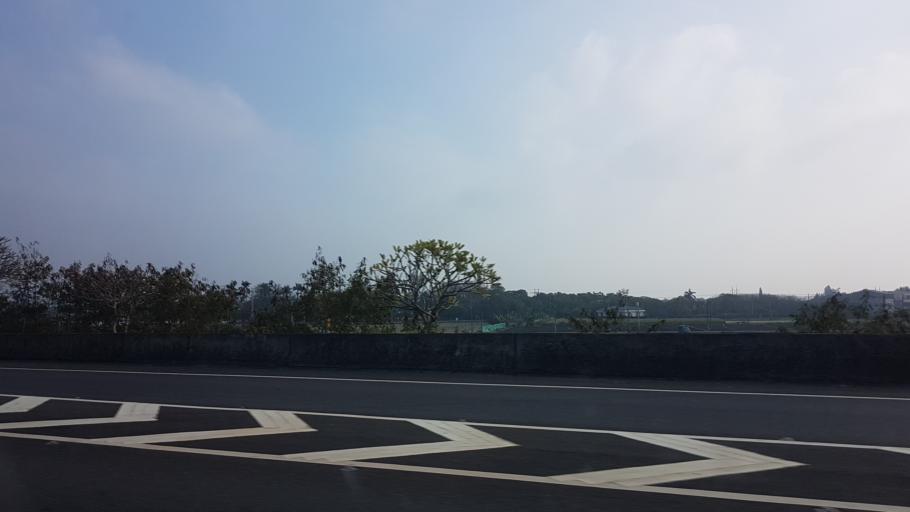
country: TW
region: Taiwan
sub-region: Chiayi
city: Taibao
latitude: 23.4196
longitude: 120.3806
